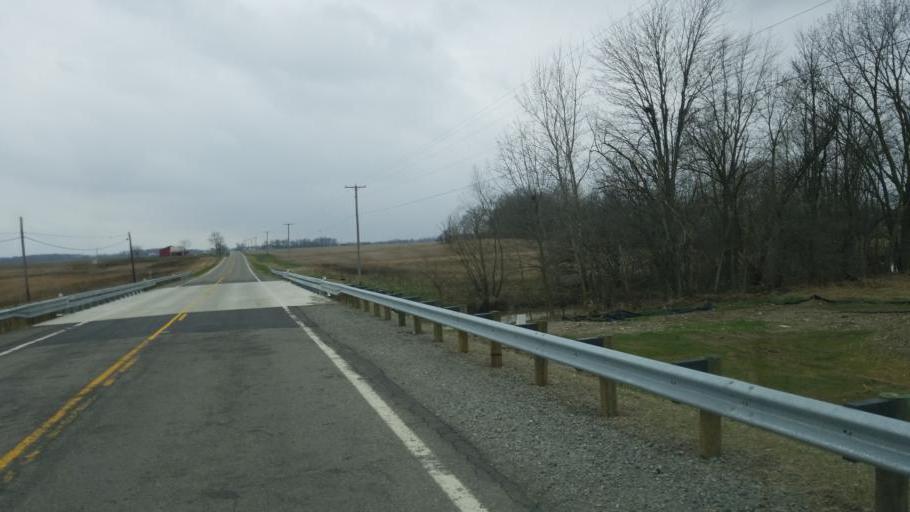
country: US
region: Ohio
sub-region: Union County
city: Richwood
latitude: 40.4098
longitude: -83.3623
